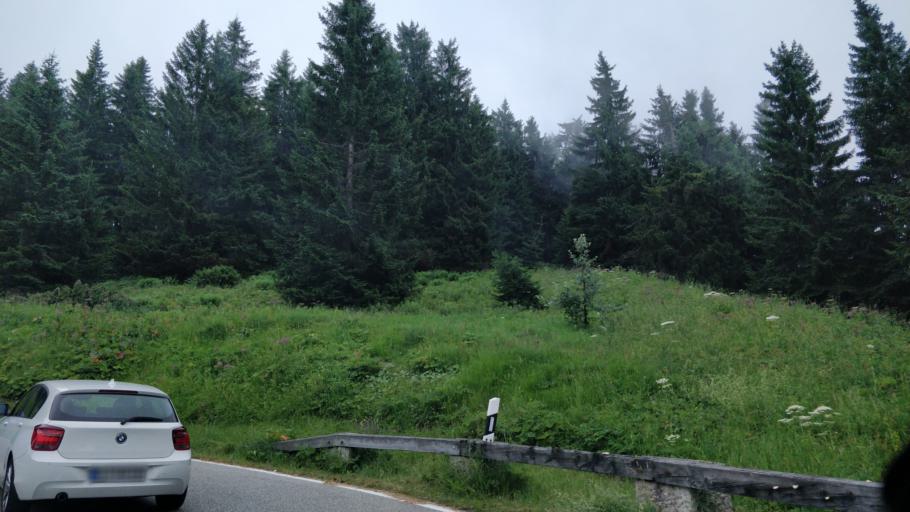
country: AT
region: Salzburg
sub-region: Politischer Bezirk Hallein
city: Kuchl
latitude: 47.6281
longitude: 13.0911
